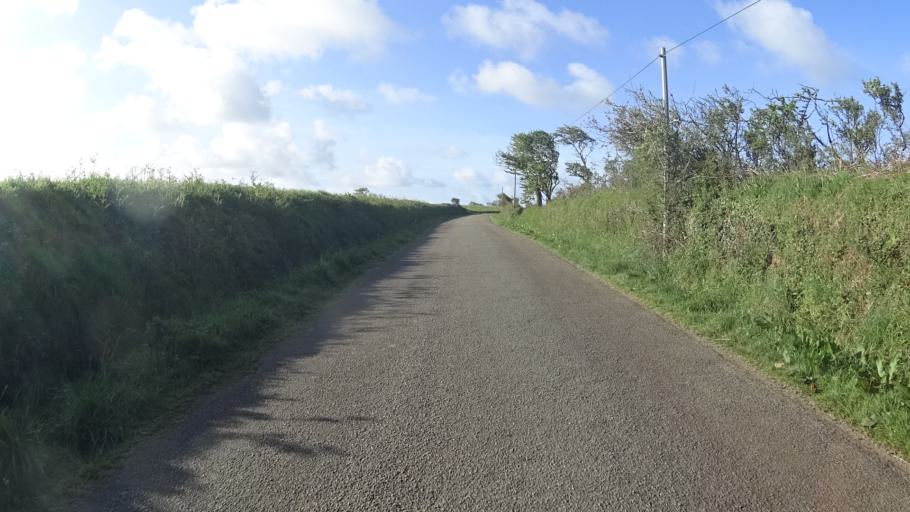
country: FR
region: Brittany
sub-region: Departement du Finistere
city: Ploumoguer
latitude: 48.4209
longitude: -4.6889
